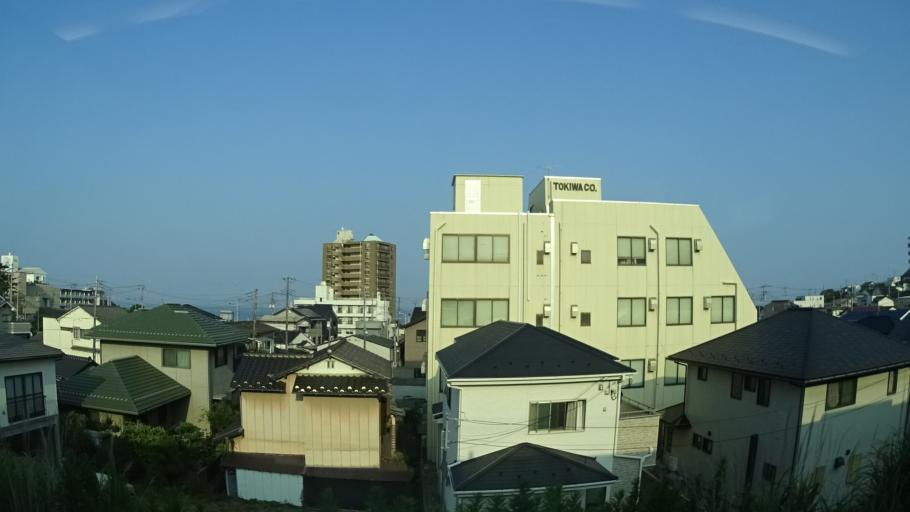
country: JP
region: Ibaraki
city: Hitachi
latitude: 36.5862
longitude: 140.6599
